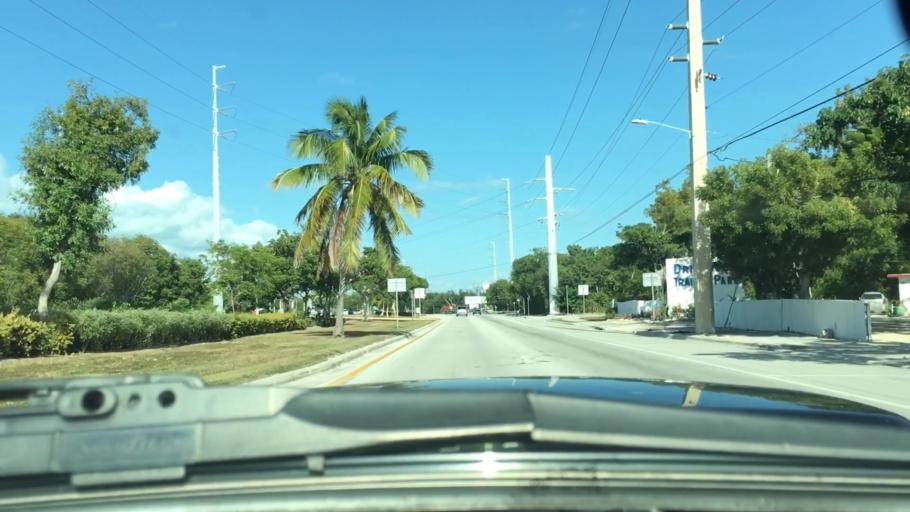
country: US
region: Florida
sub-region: Monroe County
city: Tavernier
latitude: 25.0120
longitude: -80.5143
